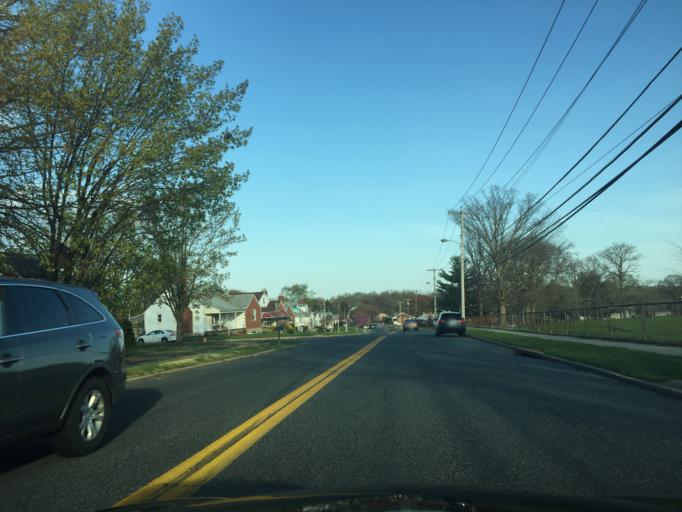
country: US
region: Maryland
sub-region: Baltimore County
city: Perry Hall
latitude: 39.4004
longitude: -76.4754
